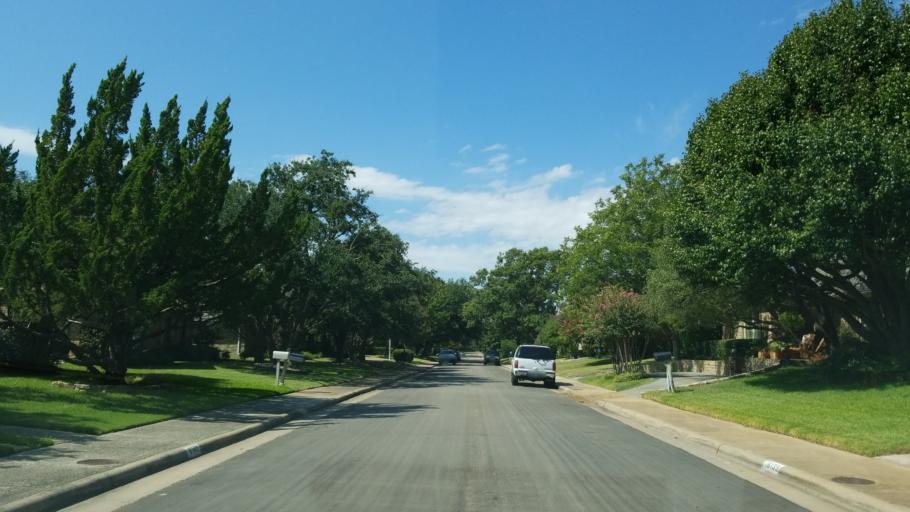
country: US
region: Texas
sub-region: Dallas County
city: Addison
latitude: 32.9588
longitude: -96.8000
